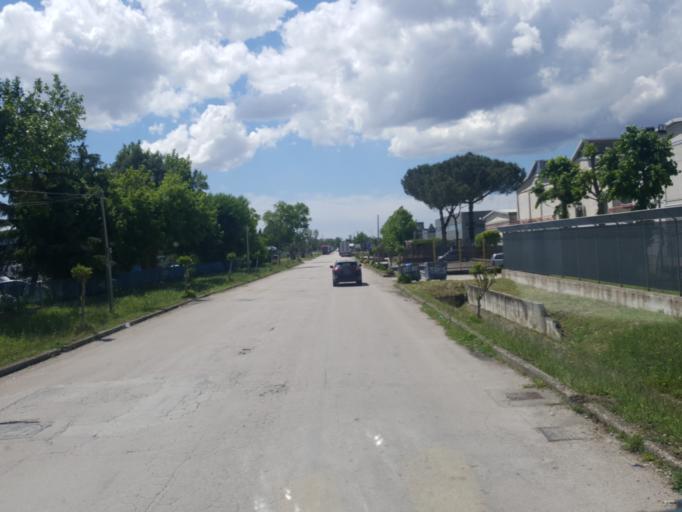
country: IT
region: Campania
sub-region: Provincia di Napoli
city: Pascarola
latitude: 40.9858
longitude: 14.3016
